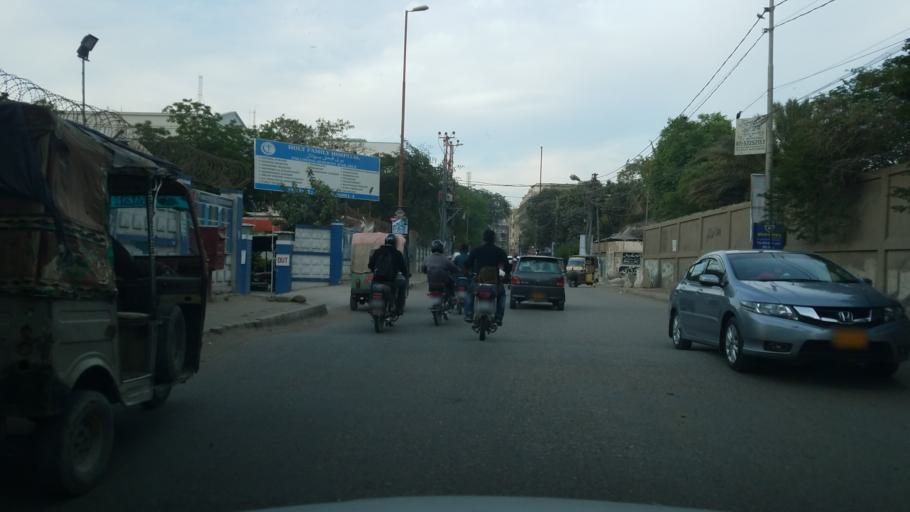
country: PK
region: Sindh
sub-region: Karachi District
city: Karachi
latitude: 24.8718
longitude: 67.0284
